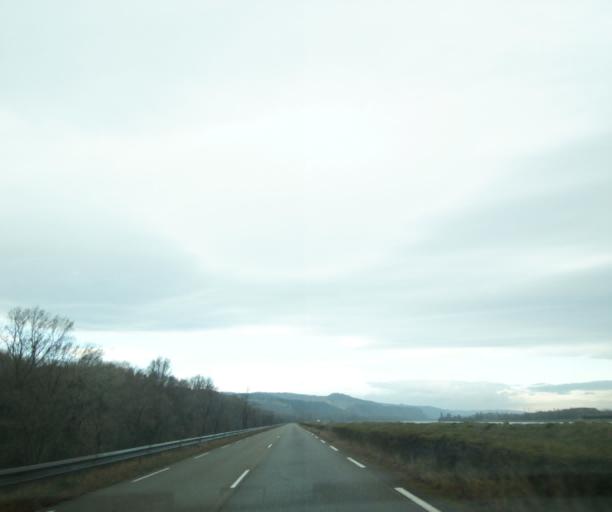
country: FR
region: Rhone-Alpes
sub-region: Departement de l'Ardeche
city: Cornas
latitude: 44.9626
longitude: 4.8678
